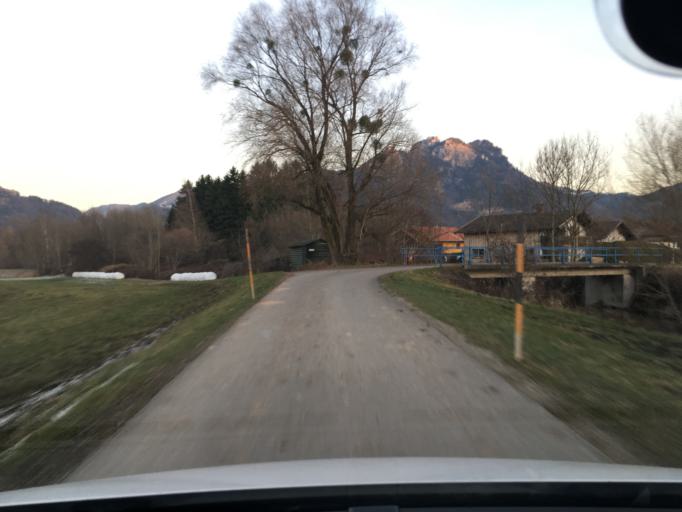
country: DE
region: Bavaria
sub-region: Upper Bavaria
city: Flintsbach
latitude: 47.7401
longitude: 12.1293
